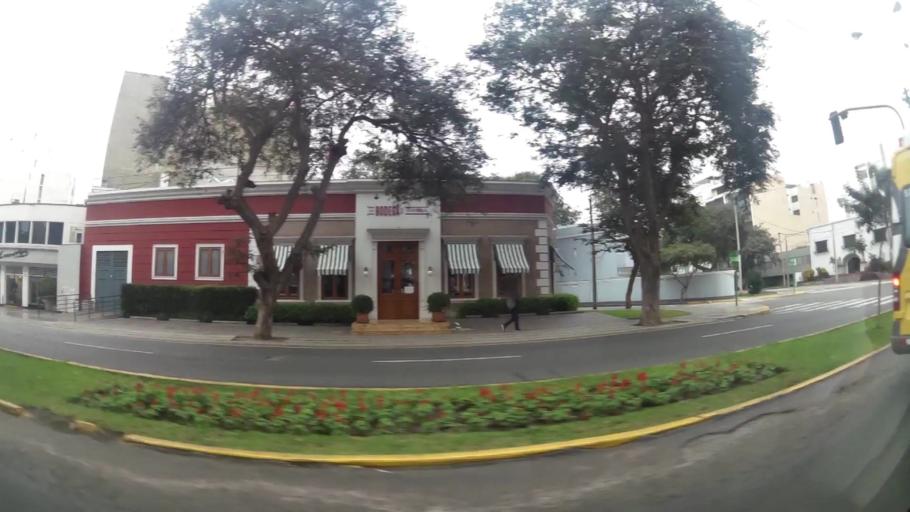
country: PE
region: Lima
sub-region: Lima
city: Surco
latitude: -12.1331
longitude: -77.0280
